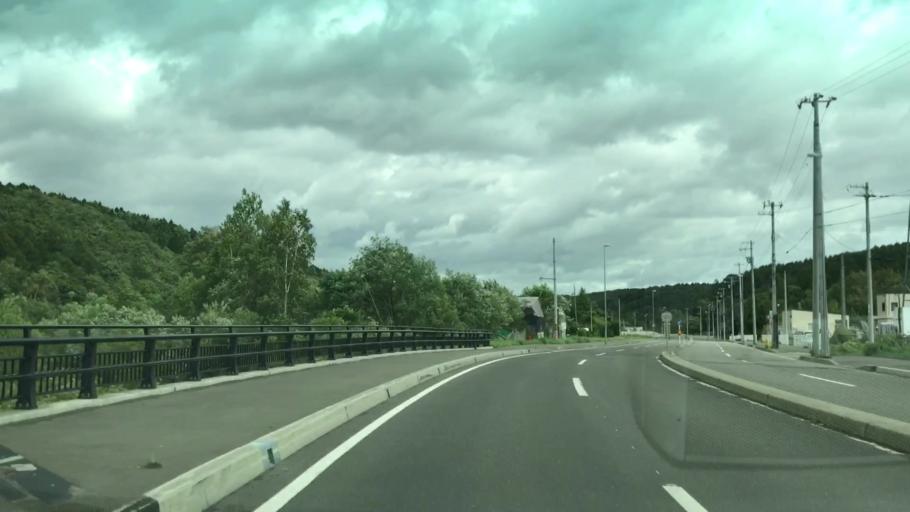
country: JP
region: Hokkaido
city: Kitahiroshima
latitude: 42.9530
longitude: 141.4515
